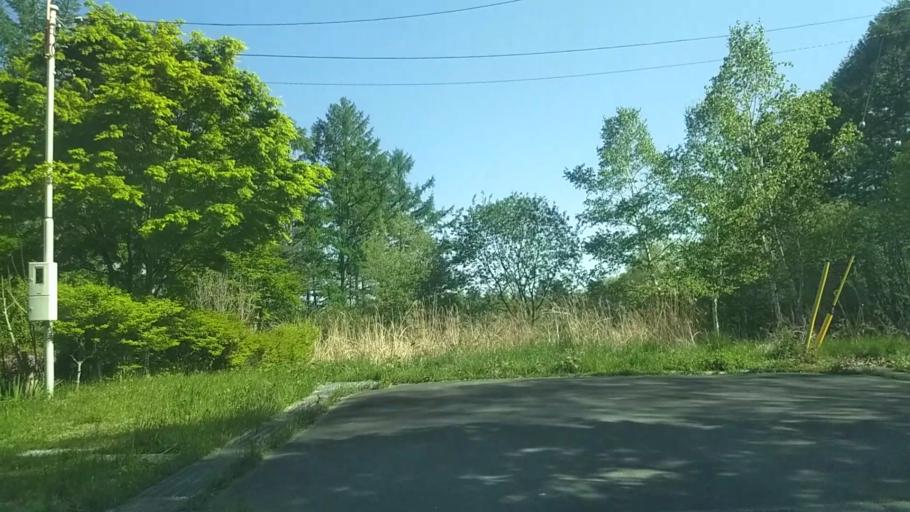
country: JP
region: Yamanashi
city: Nirasaki
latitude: 35.9064
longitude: 138.4098
